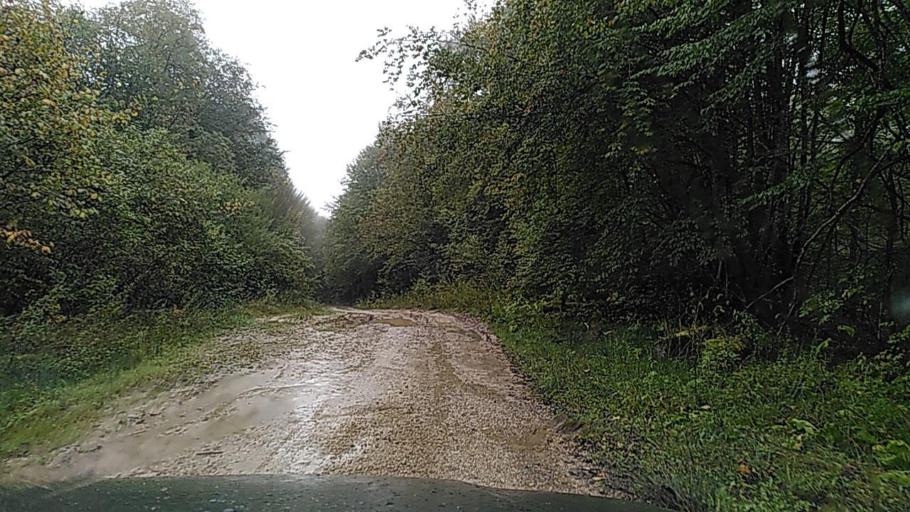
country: RU
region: Kabardino-Balkariya
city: Belaya Rechka
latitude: 43.3680
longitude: 43.4217
